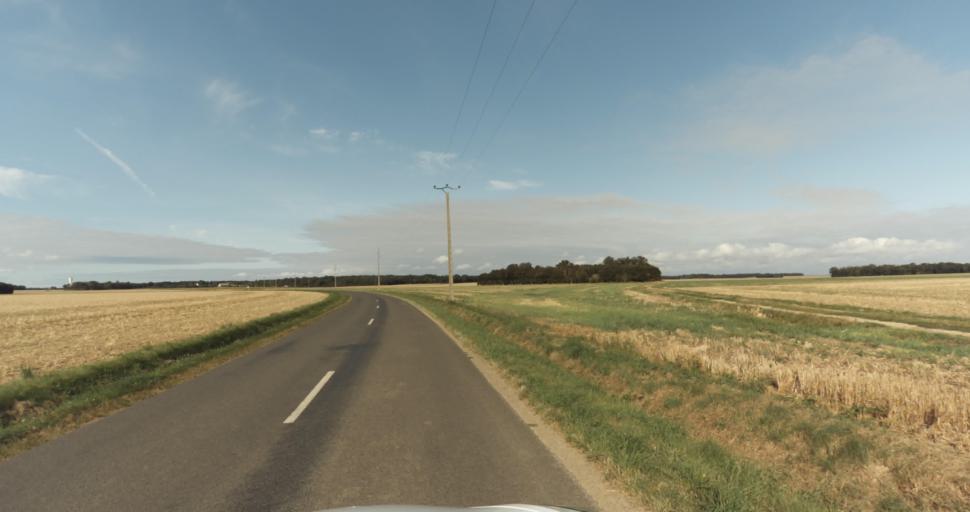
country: FR
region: Haute-Normandie
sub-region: Departement de l'Eure
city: Nonancourt
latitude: 48.8071
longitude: 1.1320
